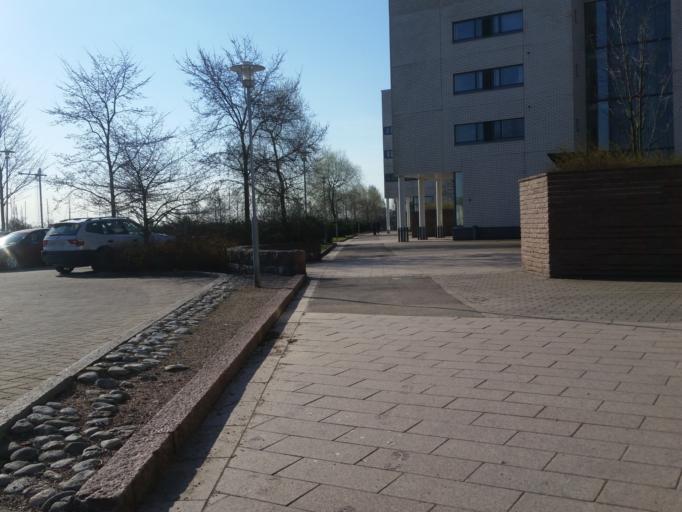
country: FI
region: Uusimaa
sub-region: Helsinki
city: Helsinki
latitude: 60.1540
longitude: 24.8875
